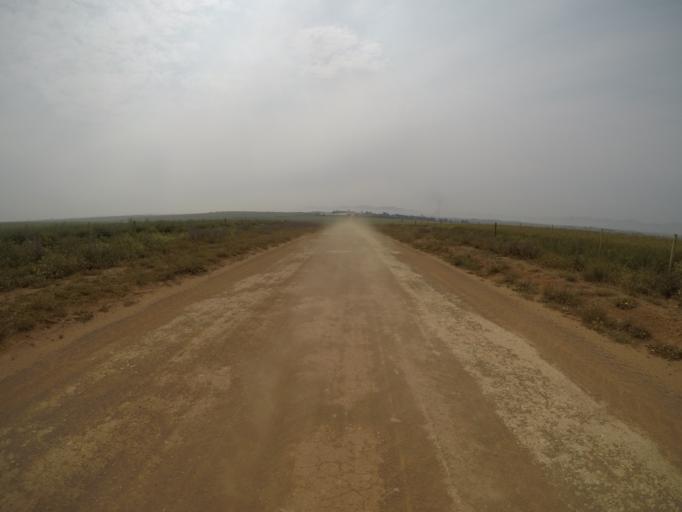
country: ZA
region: Western Cape
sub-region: City of Cape Town
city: Kraaifontein
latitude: -33.7150
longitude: 18.6834
